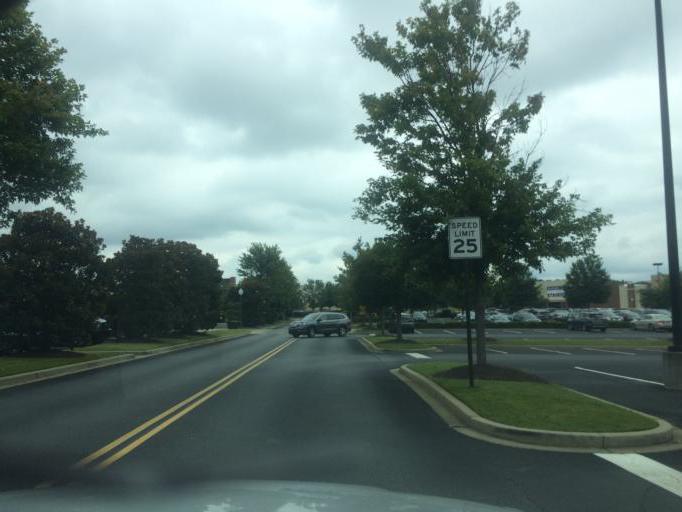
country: US
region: South Carolina
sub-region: Greenville County
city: Mauldin
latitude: 34.8292
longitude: -82.2972
